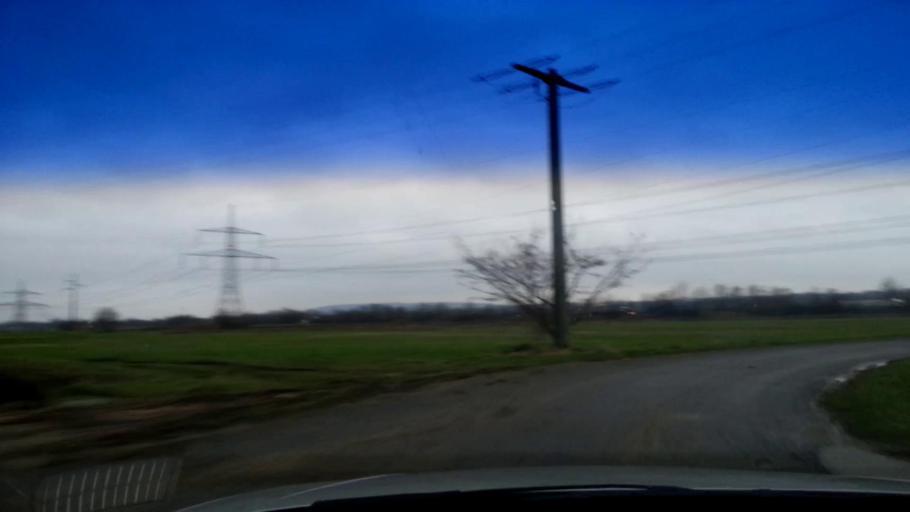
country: DE
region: Bavaria
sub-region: Upper Franconia
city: Oberhaid
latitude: 49.9272
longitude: 10.8165
